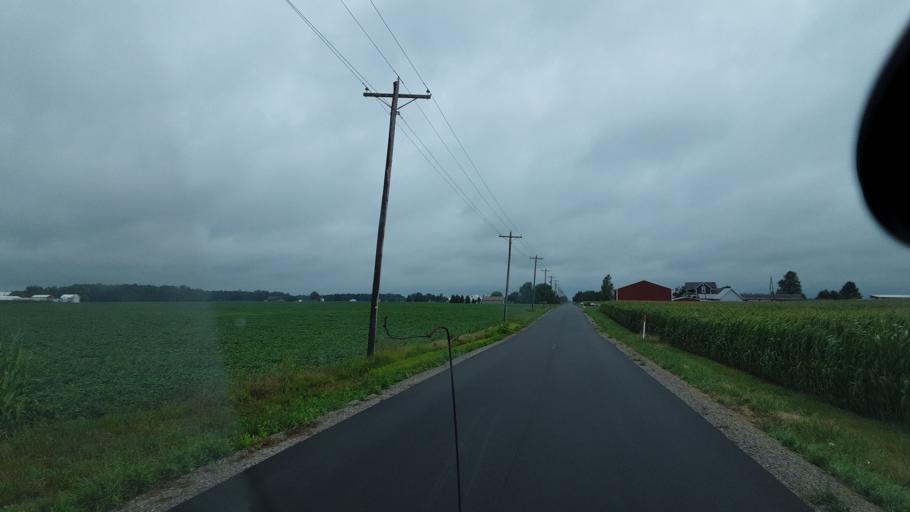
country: US
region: Indiana
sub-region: Adams County
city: Decatur
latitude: 40.8426
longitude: -84.8426
